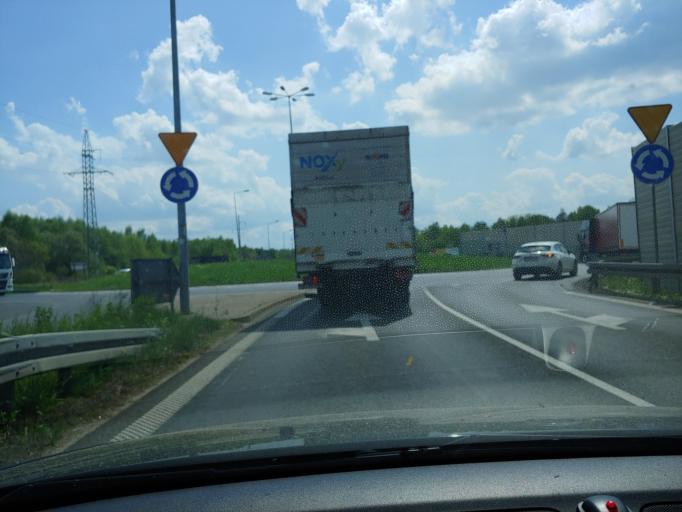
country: PL
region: Lesser Poland Voivodeship
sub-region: Powiat tarnowski
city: Tarnow
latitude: 50.0491
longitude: 21.0109
